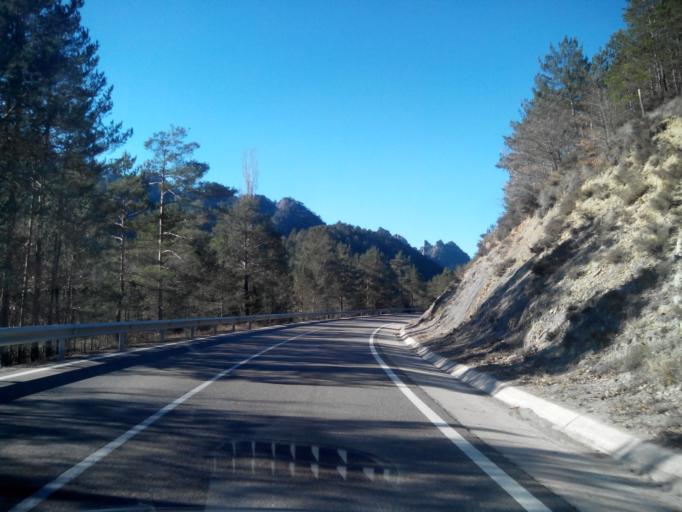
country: ES
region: Catalonia
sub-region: Provincia de Barcelona
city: Capolat
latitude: 42.1261
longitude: 1.6601
